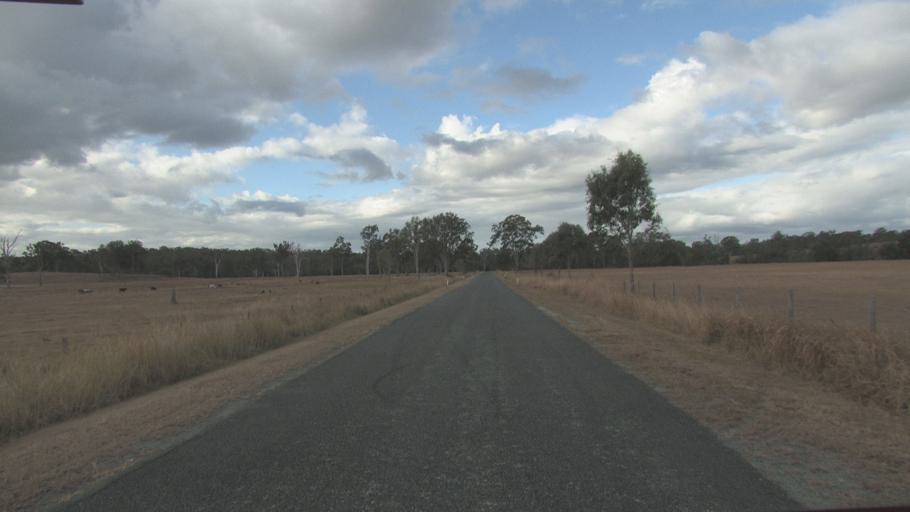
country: AU
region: Queensland
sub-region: Logan
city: Cedar Vale
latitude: -27.8885
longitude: 153.0706
